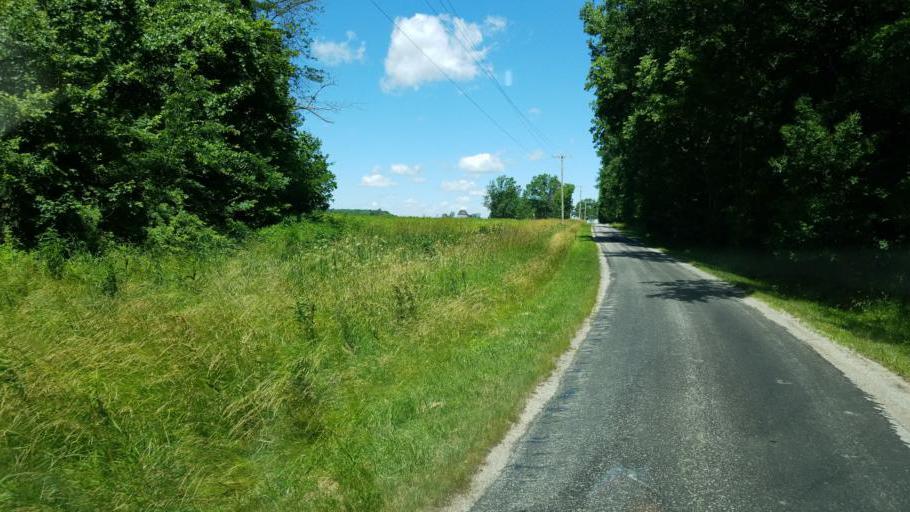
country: US
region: Ohio
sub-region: Crawford County
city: Bucyrus
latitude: 40.7284
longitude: -82.9195
